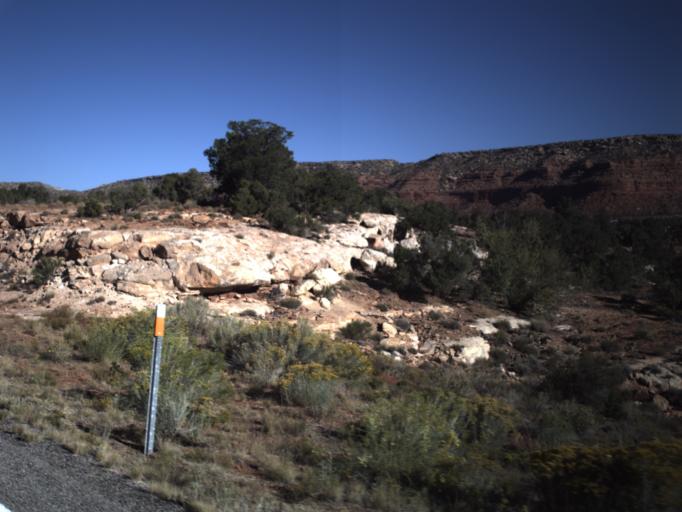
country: US
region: Utah
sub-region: San Juan County
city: Blanding
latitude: 37.6498
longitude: -110.1195
